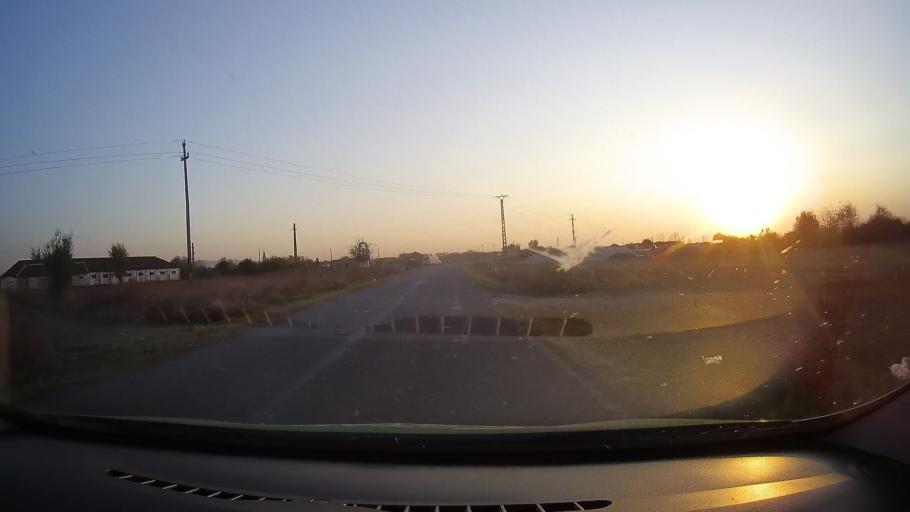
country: RO
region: Arad
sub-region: Comuna Seleus
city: Seleus
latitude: 46.3904
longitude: 21.7115
